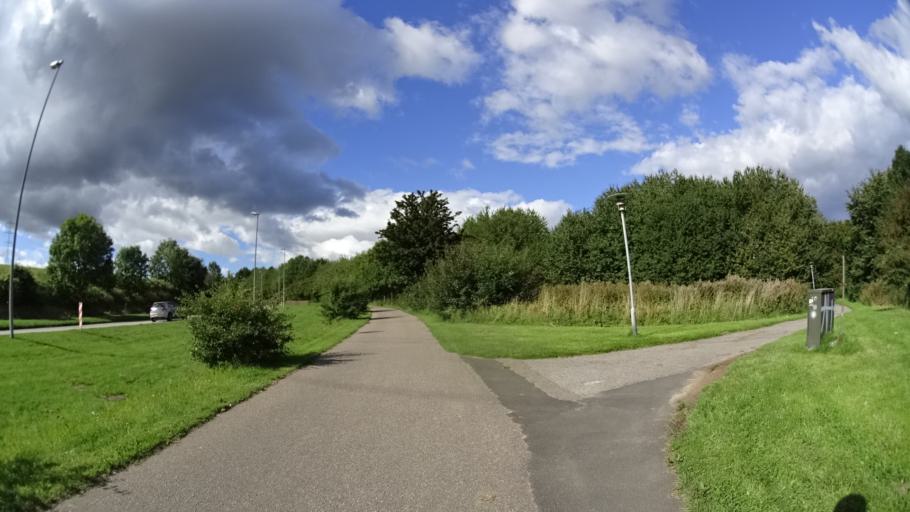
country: DK
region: Central Jutland
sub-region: Arhus Kommune
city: Stavtrup
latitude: 56.1284
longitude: 10.1317
